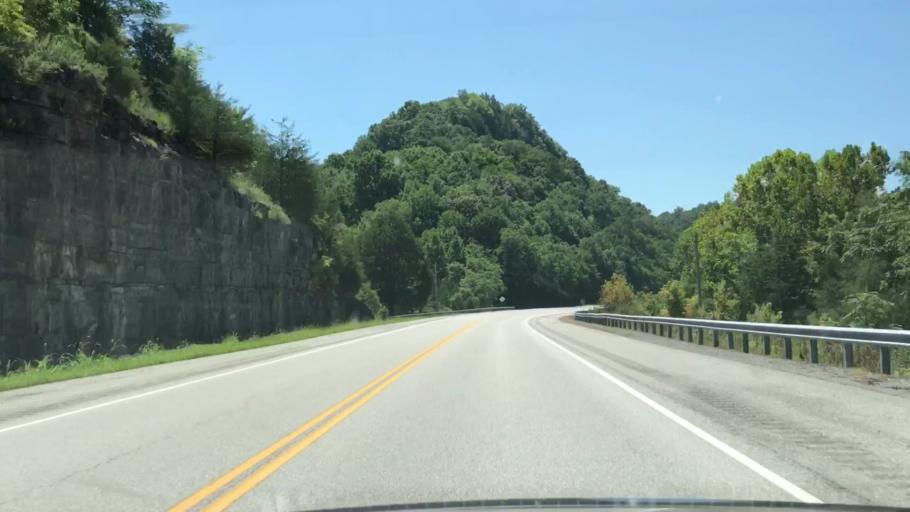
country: US
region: Tennessee
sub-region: Clay County
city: Celina
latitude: 36.4499
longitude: -85.5779
